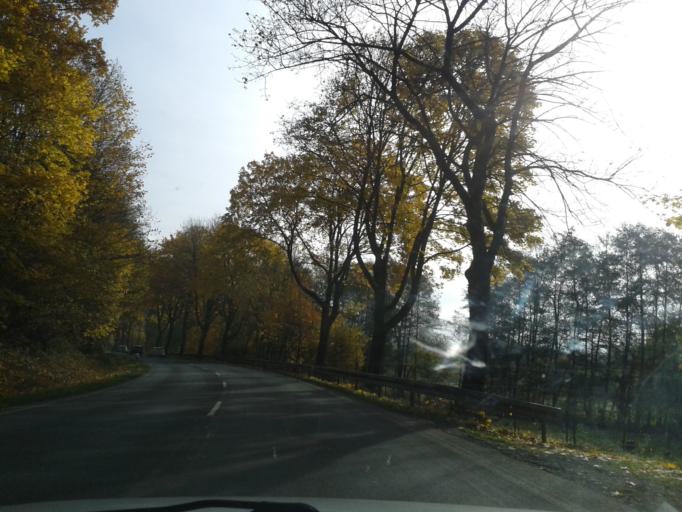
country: DE
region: North Rhine-Westphalia
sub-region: Regierungsbezirk Arnsberg
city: Olsberg
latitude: 51.3154
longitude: 8.4996
